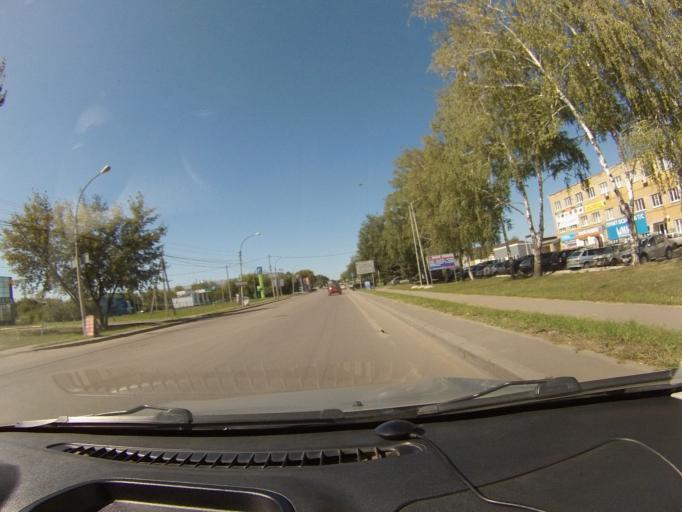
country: RU
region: Tambov
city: Donskoye
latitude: 52.7580
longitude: 41.4681
